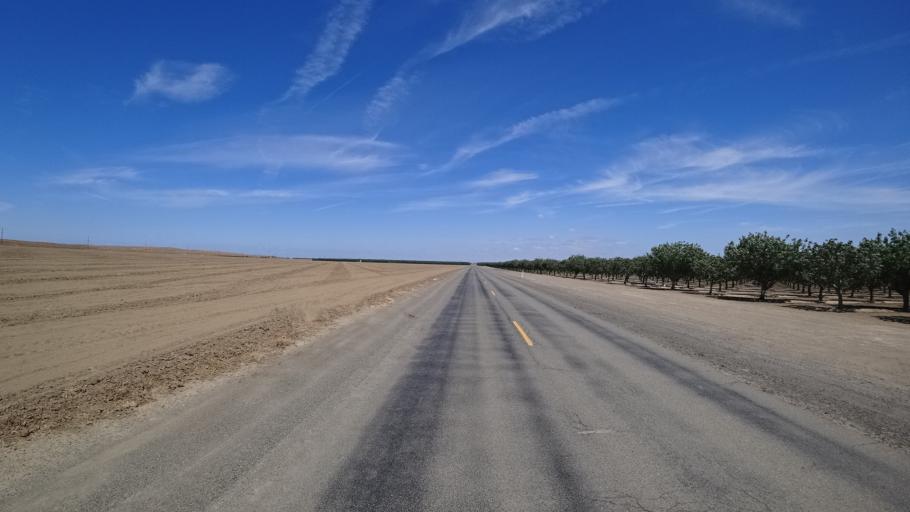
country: US
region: California
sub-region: Kings County
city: Kettleman City
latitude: 35.9205
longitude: -119.9150
